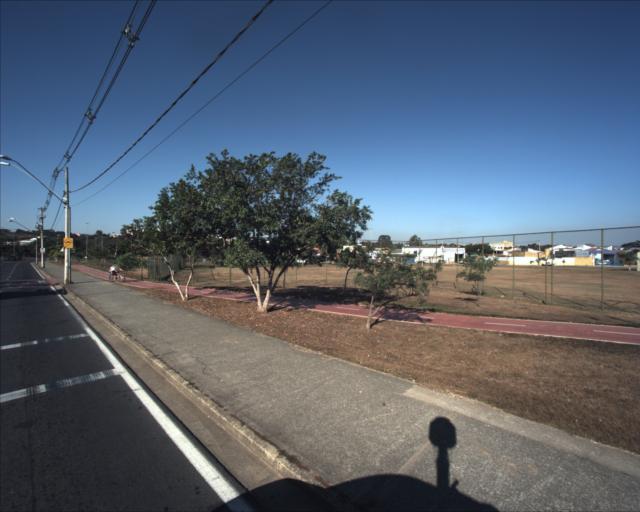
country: BR
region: Sao Paulo
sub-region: Sorocaba
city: Sorocaba
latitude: -23.4681
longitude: -47.4444
